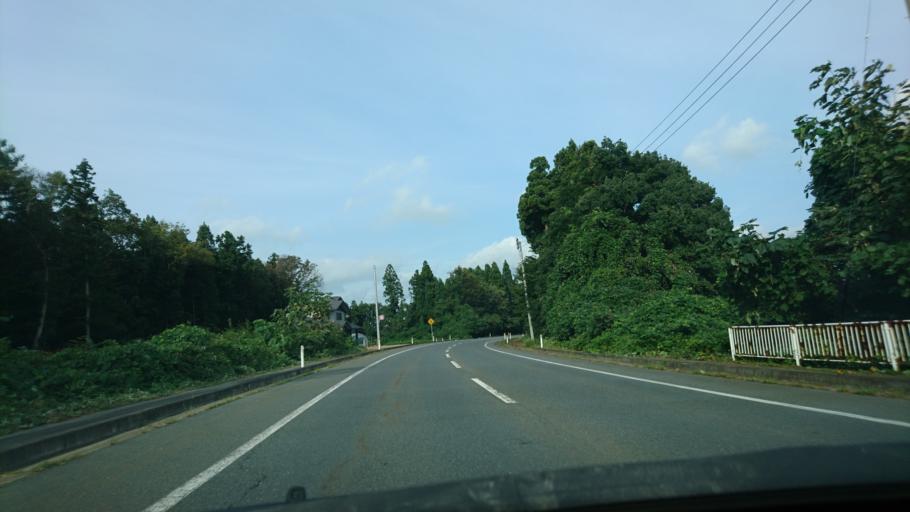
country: JP
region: Iwate
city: Kitakami
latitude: 39.3046
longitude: 141.0259
